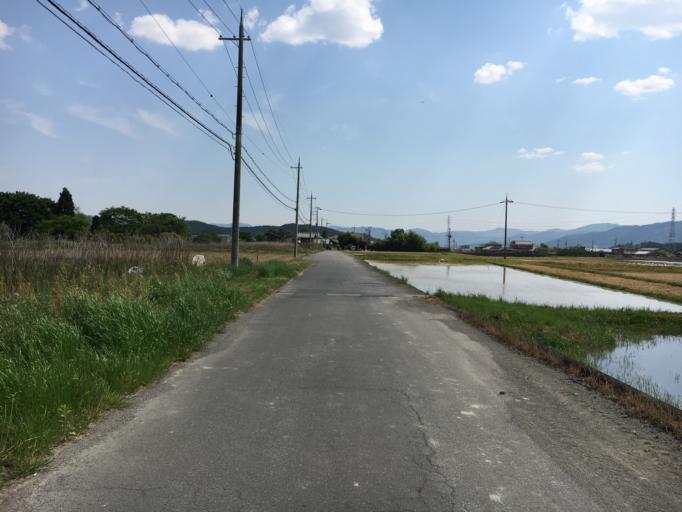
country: JP
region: Kyoto
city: Kameoka
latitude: 35.0819
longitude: 135.5560
